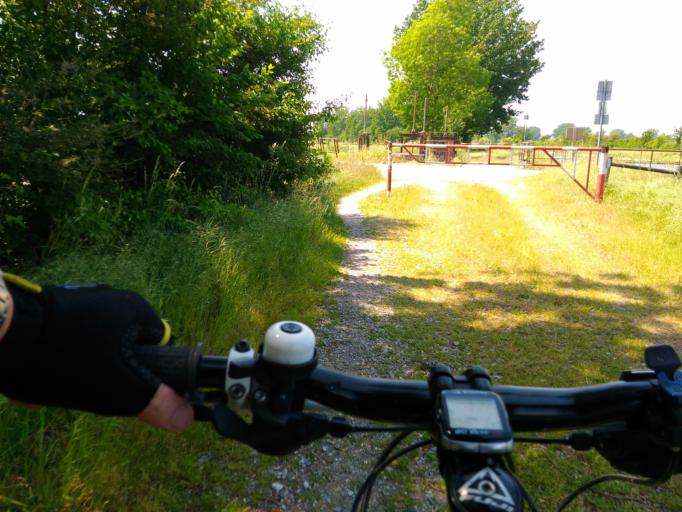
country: IT
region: Lombardy
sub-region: Provincia di Lodi
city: Montanaso Lombardo
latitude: 45.3443
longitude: 9.4695
